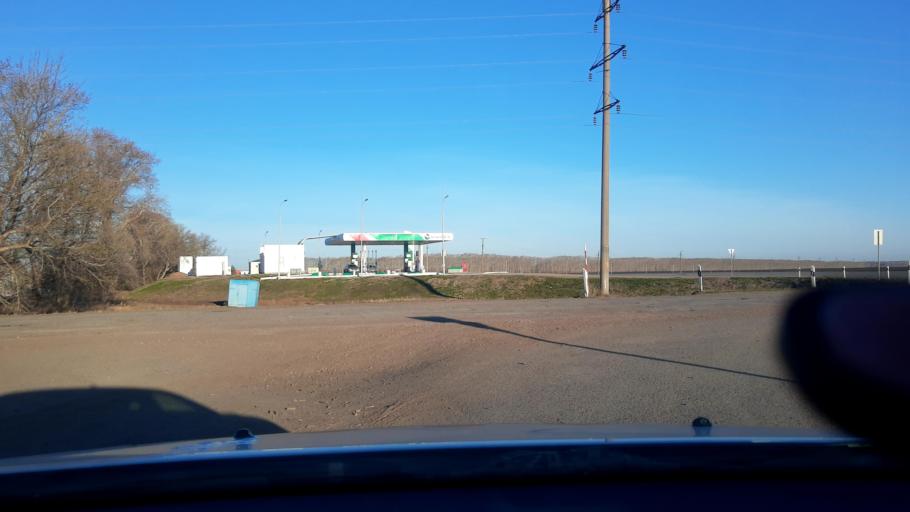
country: RU
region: Bashkortostan
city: Karmaskaly
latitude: 54.3851
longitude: 56.1904
